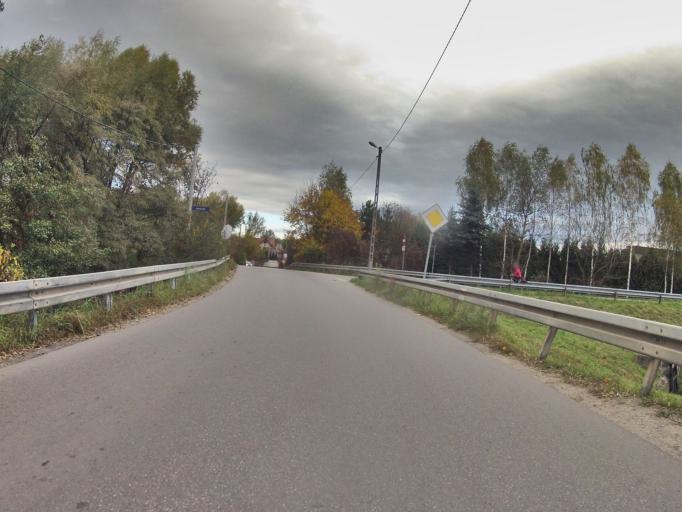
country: PL
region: Lesser Poland Voivodeship
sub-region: Powiat krakowski
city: Rzaska
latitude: 50.0708
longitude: 19.8776
